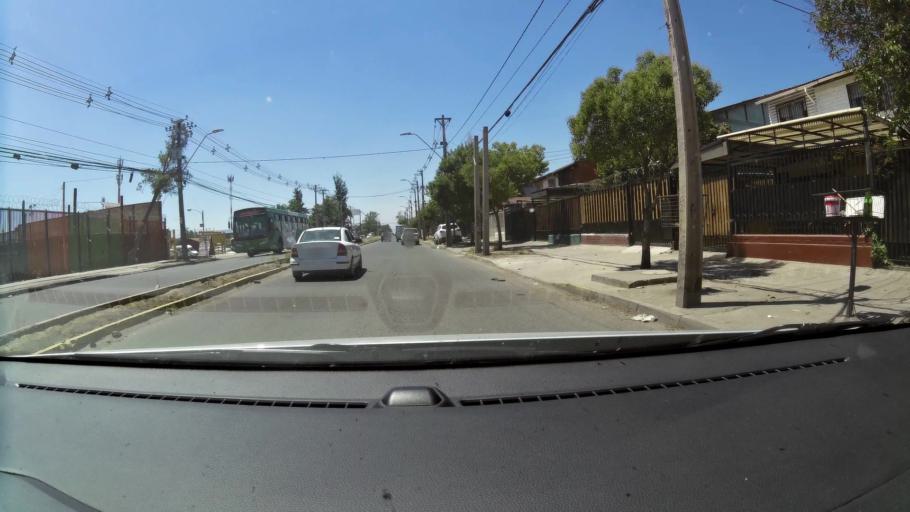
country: CL
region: Santiago Metropolitan
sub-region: Provincia de Maipo
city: San Bernardo
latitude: -33.6018
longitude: -70.6817
